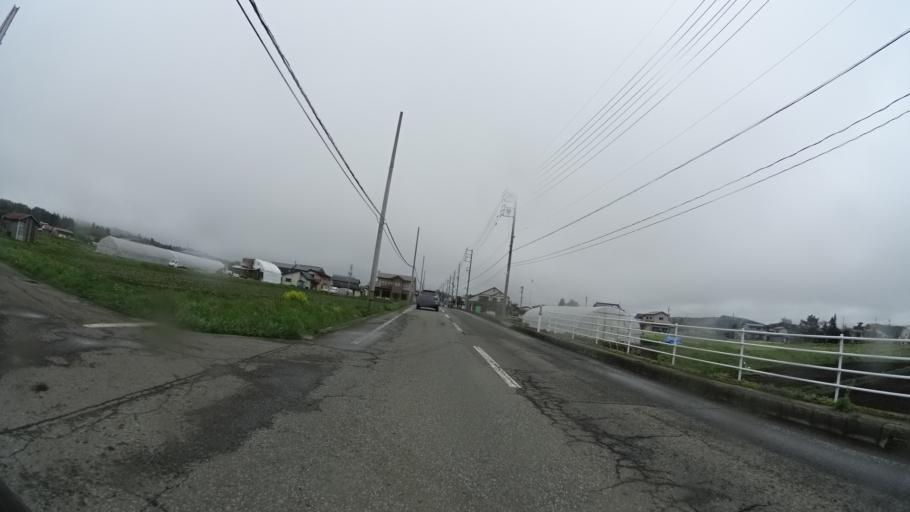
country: JP
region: Nagano
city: Nagano-shi
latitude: 36.7881
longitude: 138.1975
